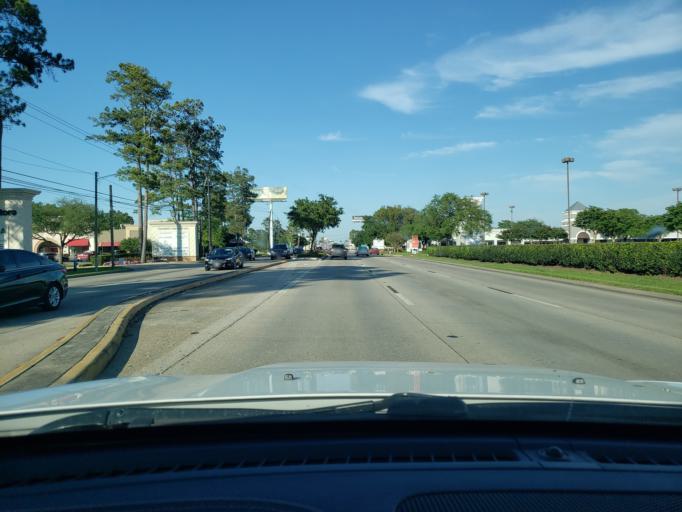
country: US
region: Texas
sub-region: Harris County
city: Hudson
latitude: 29.9801
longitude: -95.5125
